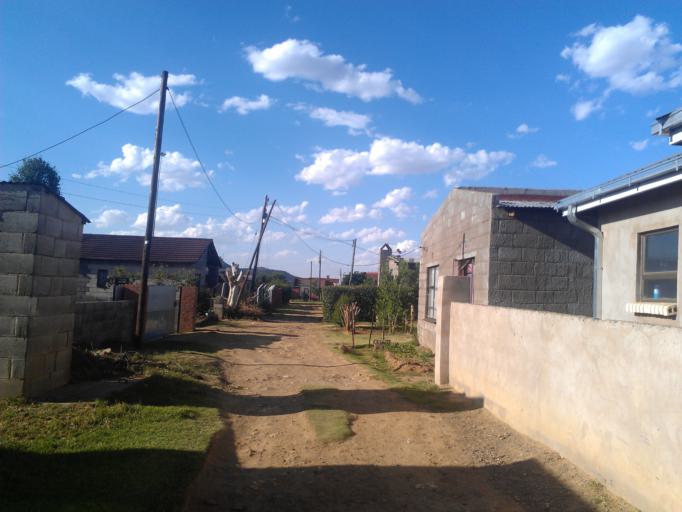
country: LS
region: Maseru
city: Maseru
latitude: -29.2865
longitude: 27.5213
